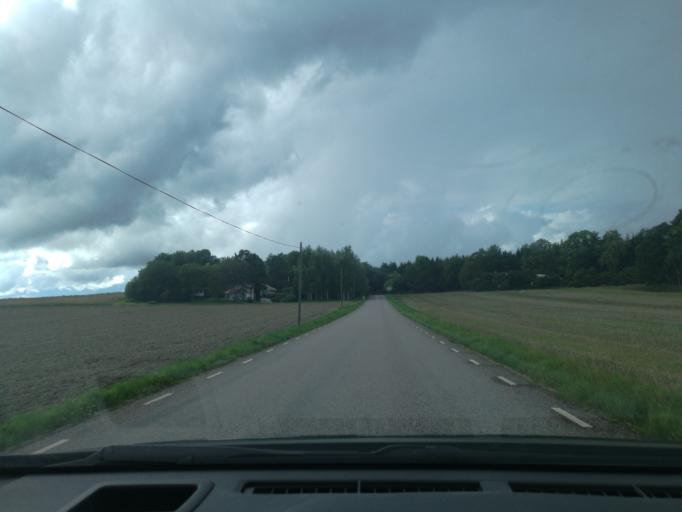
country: SE
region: OEstergoetland
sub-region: Soderkopings Kommun
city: Soederkoeping
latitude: 58.5292
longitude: 16.3028
